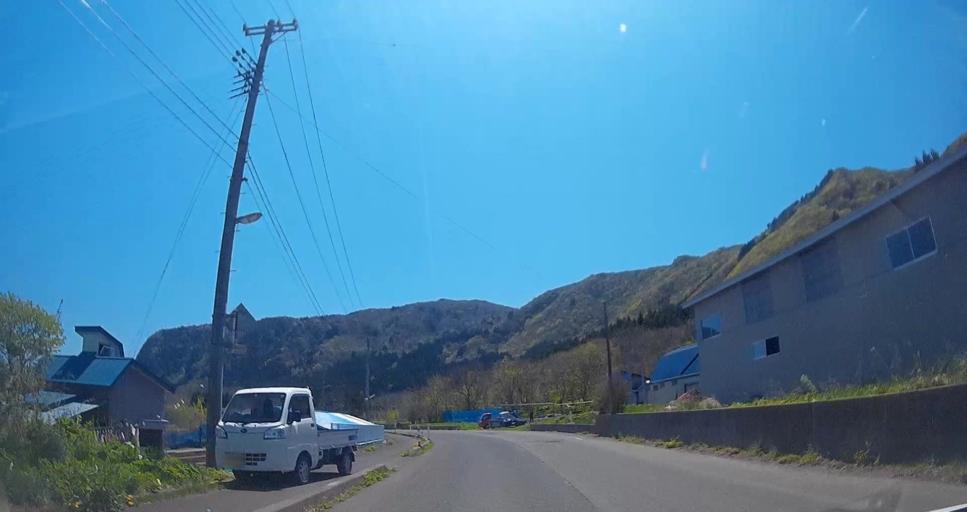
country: JP
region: Aomori
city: Mutsu
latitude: 41.4037
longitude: 141.4470
